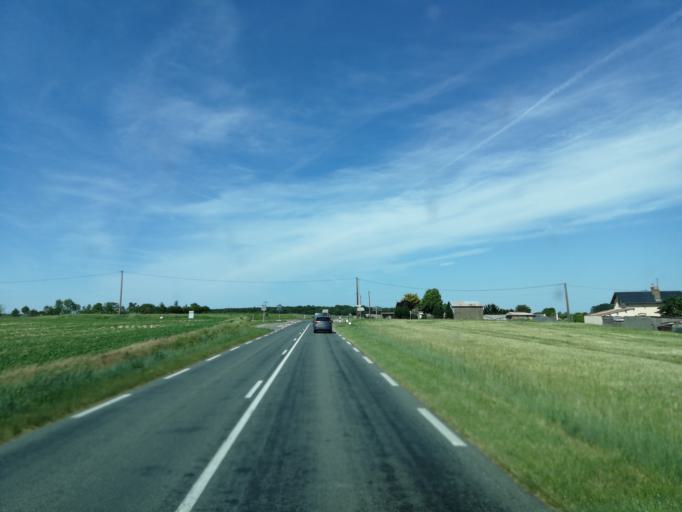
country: FR
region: Poitou-Charentes
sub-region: Departement de la Vienne
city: Loudun
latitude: 47.0343
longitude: 0.1218
